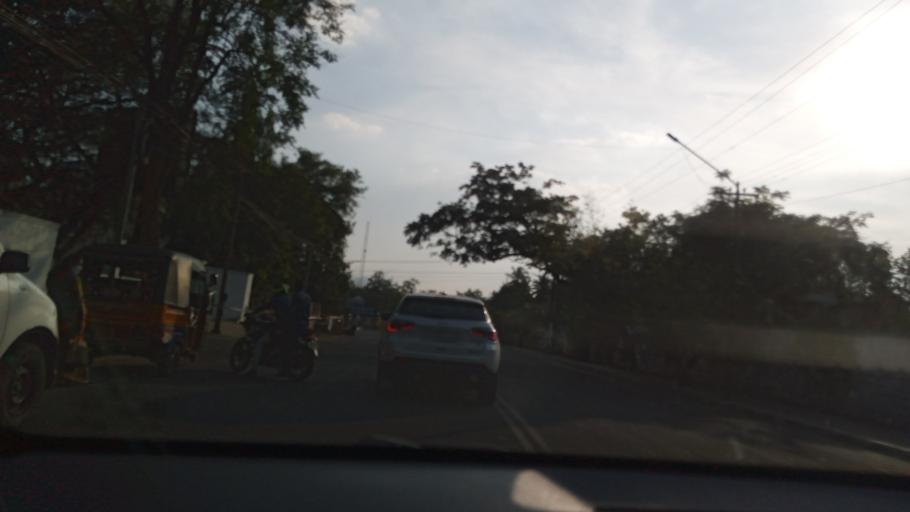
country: IN
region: Tamil Nadu
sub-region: Coimbatore
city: Coimbatore
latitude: 11.0026
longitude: 76.9720
